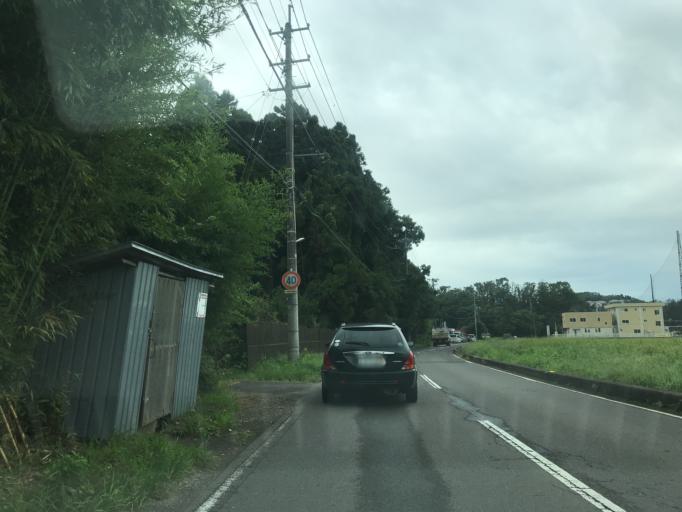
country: JP
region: Miyagi
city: Sendai-shi
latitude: 38.3192
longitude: 140.8647
